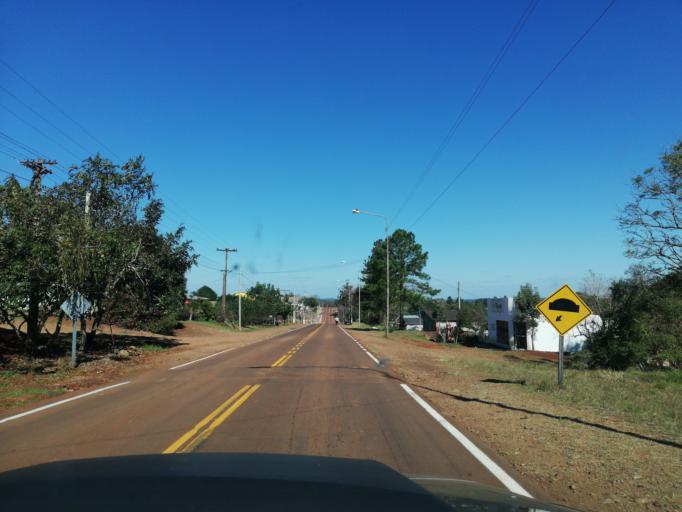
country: AR
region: Misiones
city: Aristobulo del Valle
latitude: -27.0786
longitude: -54.8316
